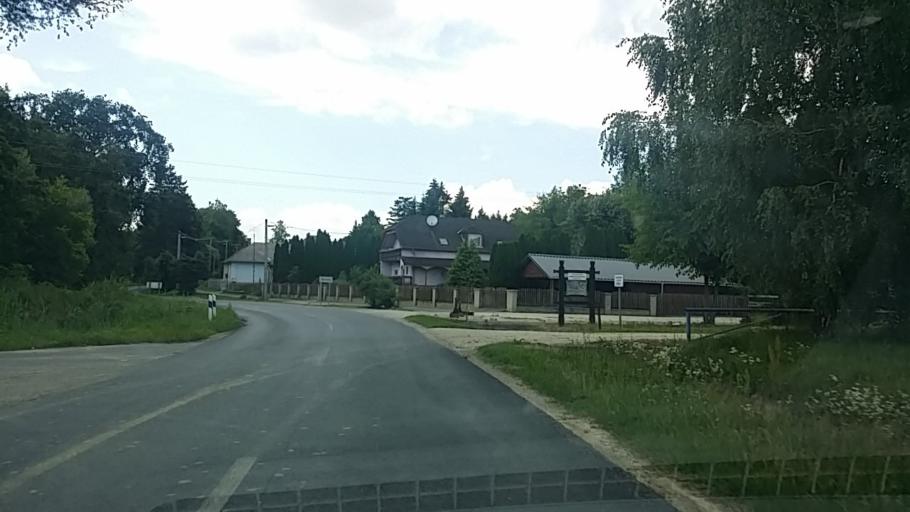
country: HU
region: Zala
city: Becsehely
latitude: 46.4945
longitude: 16.7859
